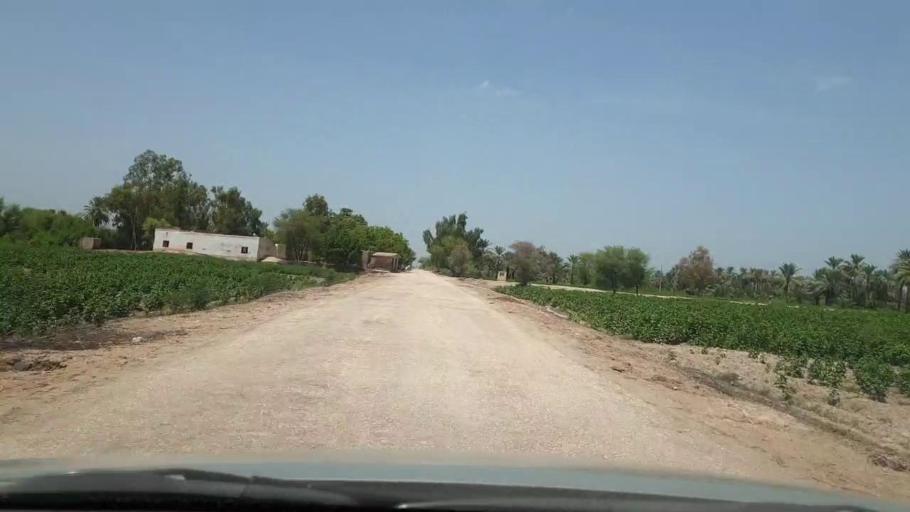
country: PK
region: Sindh
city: Pano Aqil
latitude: 27.7076
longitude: 69.2169
